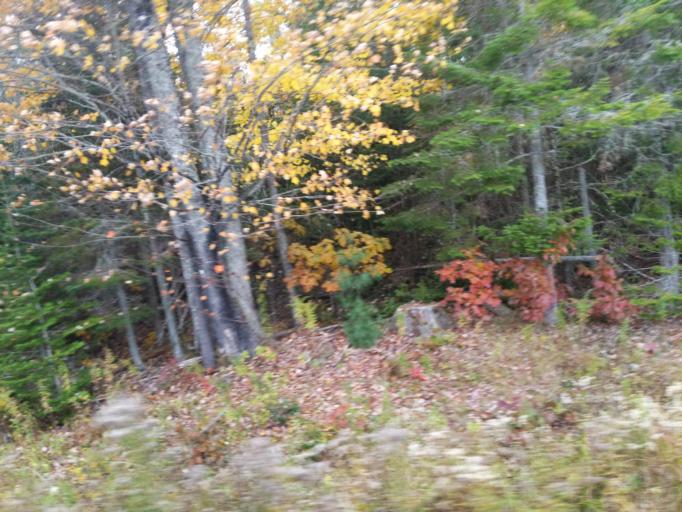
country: US
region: Maine
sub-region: Lincoln County
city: Whitefield
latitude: 44.0854
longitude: -69.6249
